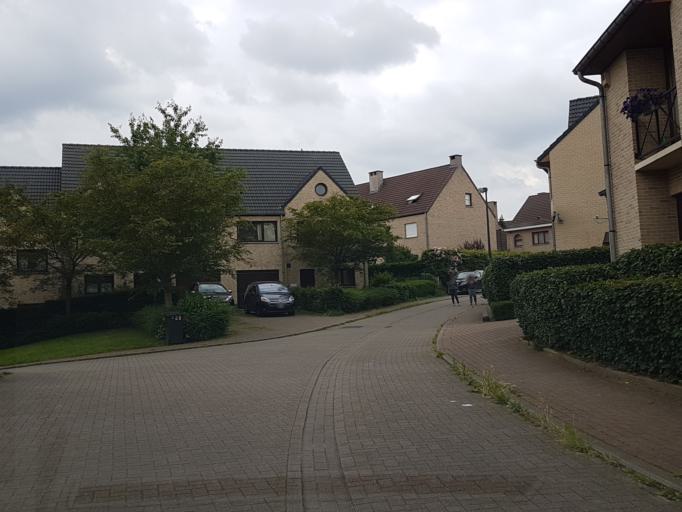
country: BE
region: Flanders
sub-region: Provincie Vlaams-Brabant
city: Kraainem
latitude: 50.8739
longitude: 4.4521
